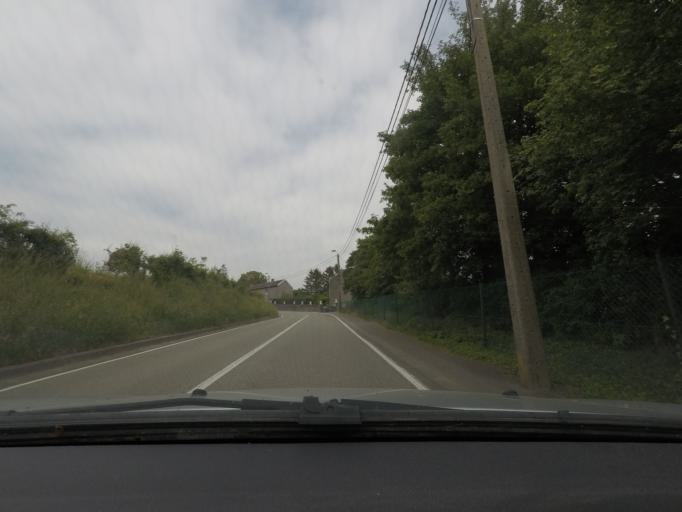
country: BE
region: Wallonia
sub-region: Province de Namur
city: Noville-les-Bois
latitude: 50.4742
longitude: 4.9974
